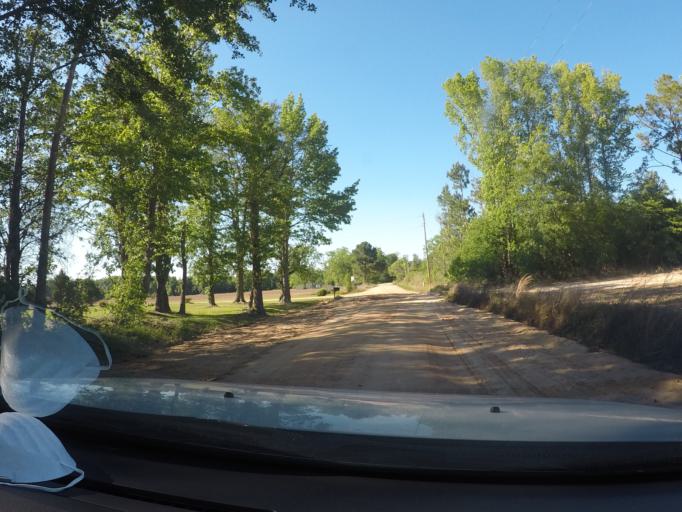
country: US
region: Georgia
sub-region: Bulloch County
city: Brooklet
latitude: 32.3141
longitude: -81.7458
